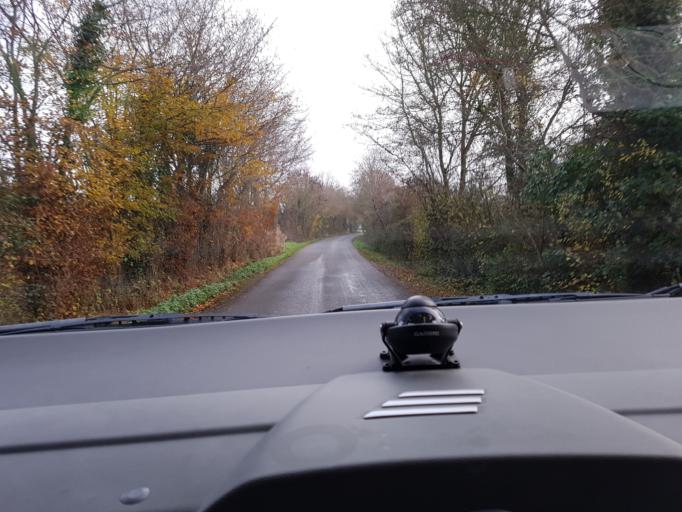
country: FR
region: Lower Normandy
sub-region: Departement de l'Orne
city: Ecouche
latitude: 48.6361
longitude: -0.0499
